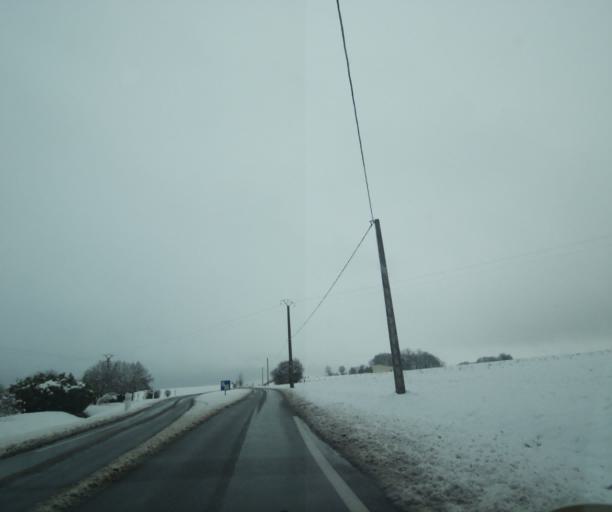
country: FR
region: Champagne-Ardenne
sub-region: Departement de la Haute-Marne
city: Montier-en-Der
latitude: 48.5310
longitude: 4.8161
